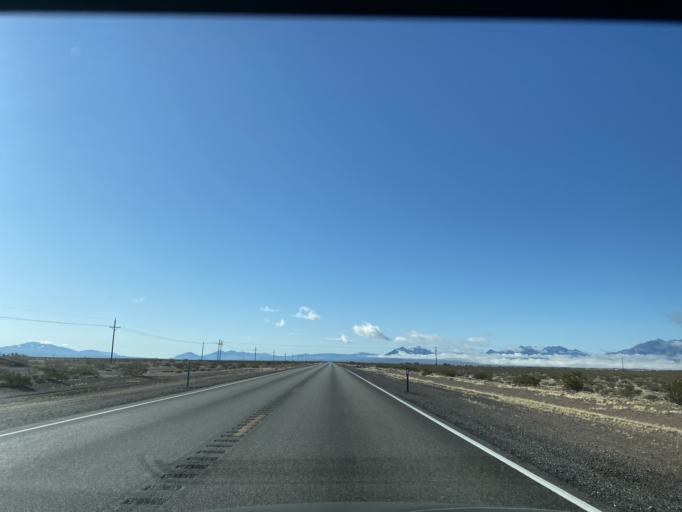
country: US
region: Nevada
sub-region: Nye County
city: Beatty
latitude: 36.5864
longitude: -116.4106
